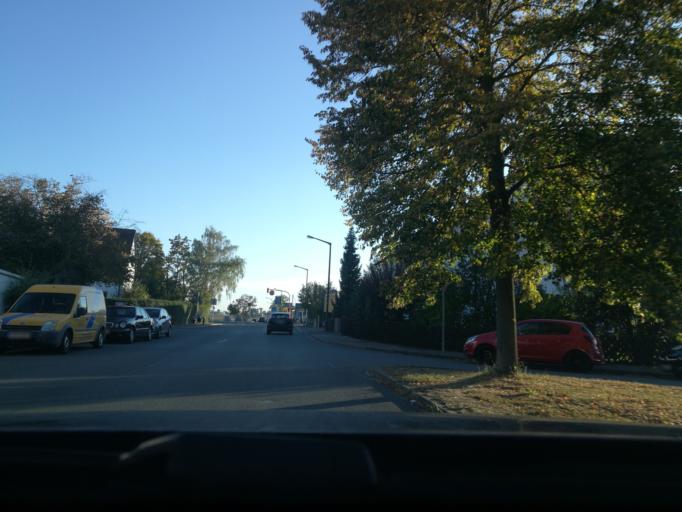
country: DE
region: Bavaria
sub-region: Regierungsbezirk Mittelfranken
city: Furth
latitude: 49.5242
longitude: 11.0075
